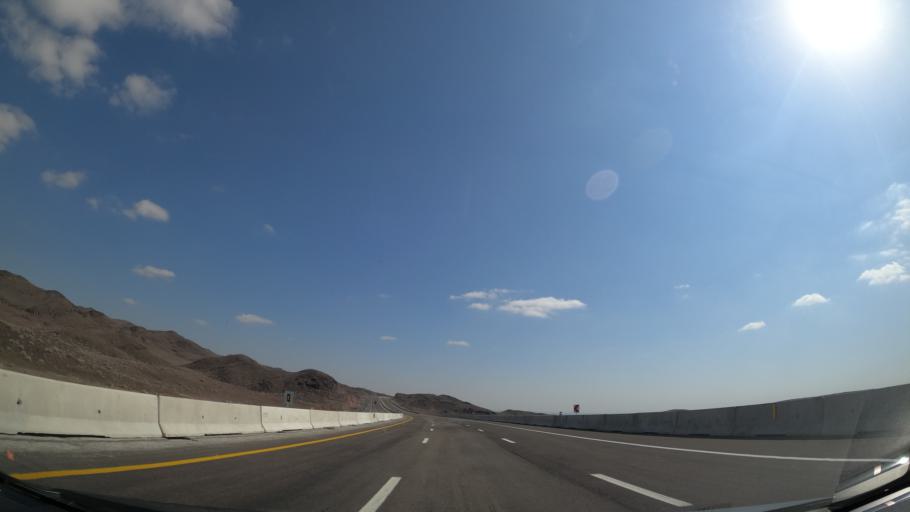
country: IR
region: Alborz
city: Eshtehard
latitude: 35.6642
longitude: 50.6499
